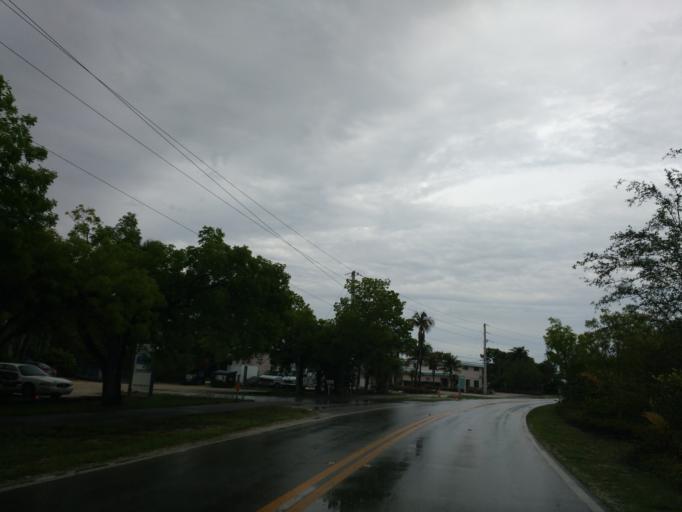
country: US
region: Florida
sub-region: Lee County
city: Sanibel
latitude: 26.4397
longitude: -82.0791
